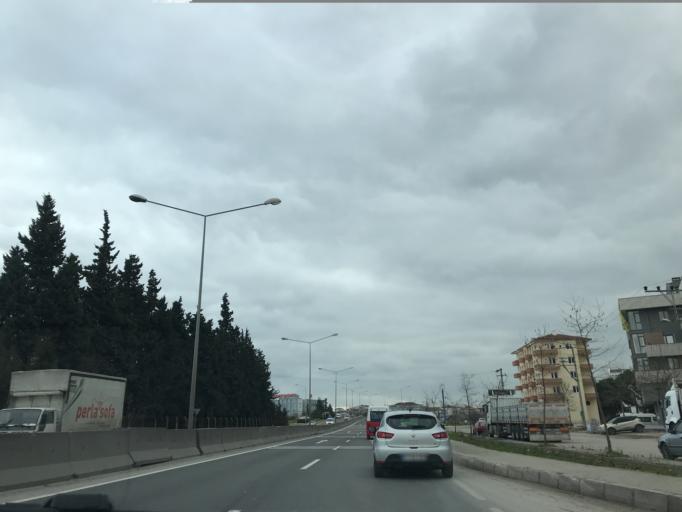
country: TR
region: Yalova
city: Ciftlikkoy
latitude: 40.6606
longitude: 29.3032
